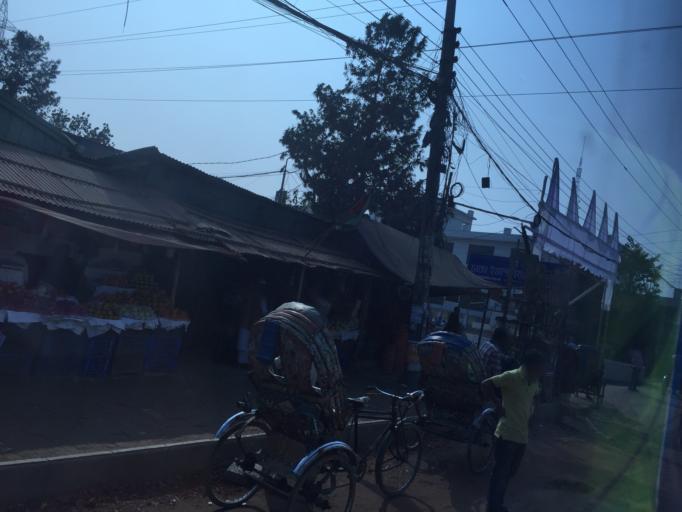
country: BD
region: Dhaka
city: Paltan
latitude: 23.7692
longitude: 90.4240
